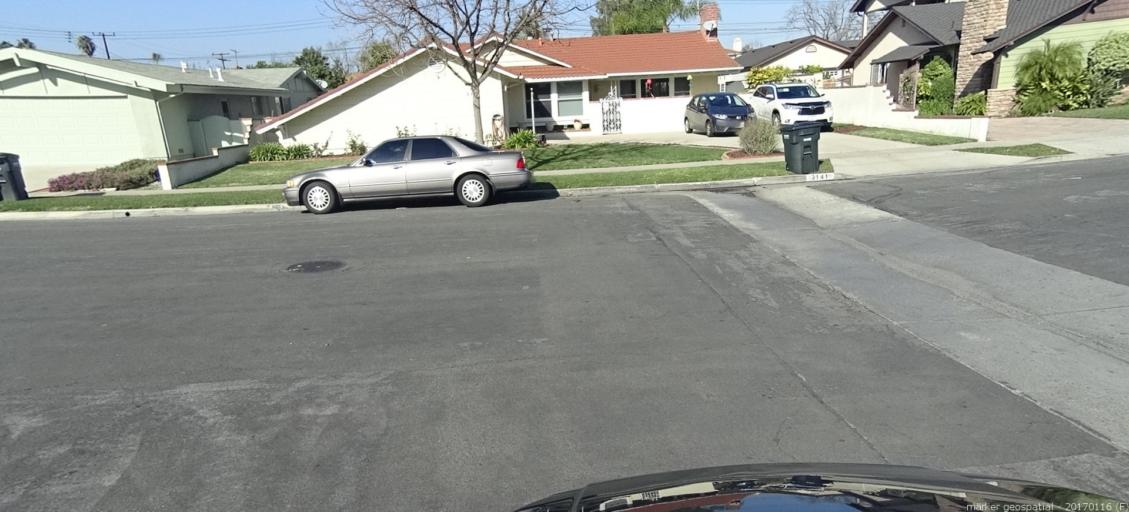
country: US
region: California
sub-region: Orange County
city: Rossmoor
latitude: 33.7830
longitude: -118.0791
